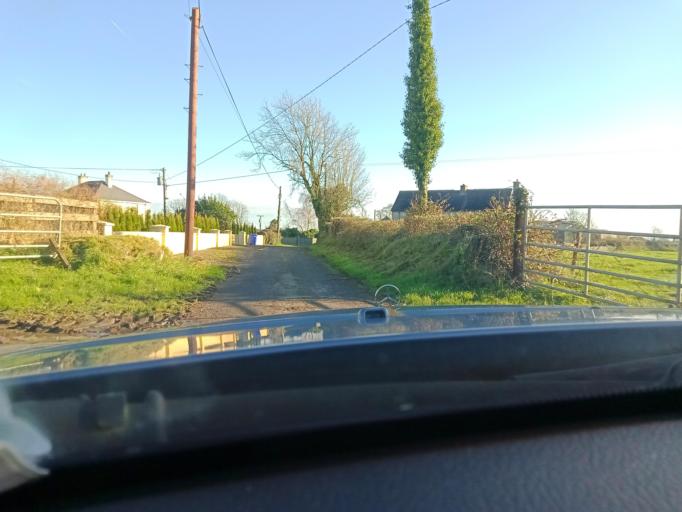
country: IE
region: Leinster
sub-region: Kilkenny
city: Mooncoin
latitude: 52.2970
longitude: -7.1901
